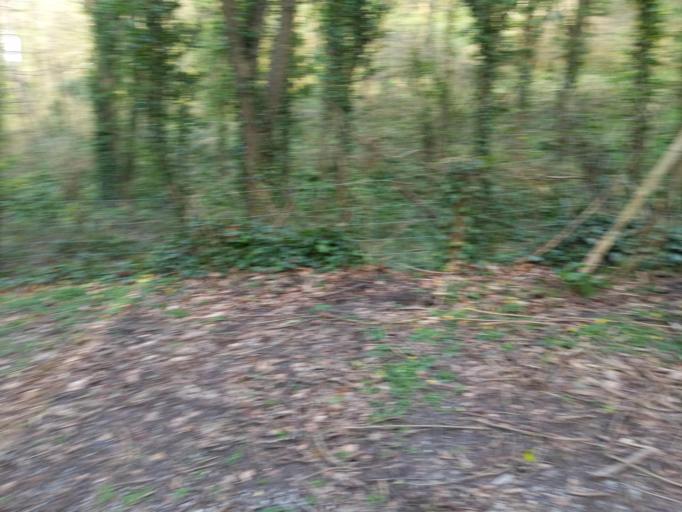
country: GB
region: England
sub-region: Devon
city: Salcombe
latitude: 50.2280
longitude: -3.7651
